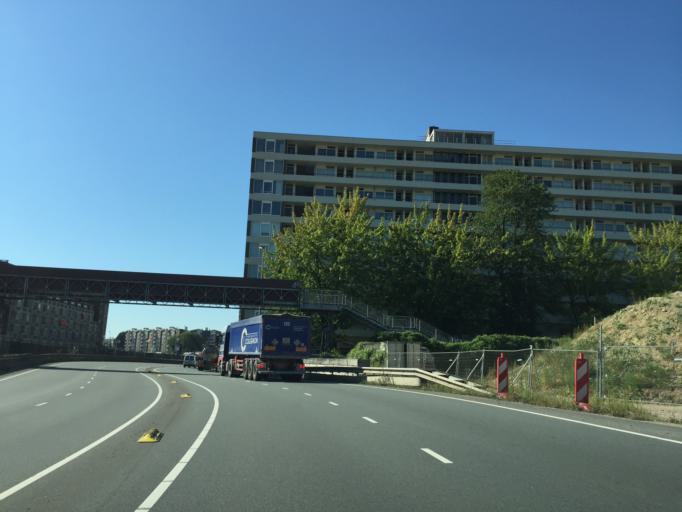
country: NL
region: Limburg
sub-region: Gemeente Maastricht
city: Maastricht
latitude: 50.8505
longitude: 5.7105
